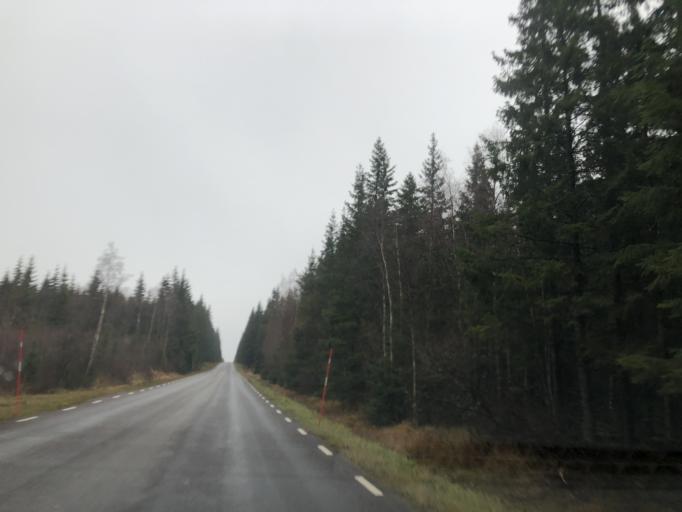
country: SE
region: Vaestra Goetaland
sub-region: Ulricehamns Kommun
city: Ulricehamn
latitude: 57.7303
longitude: 13.5457
